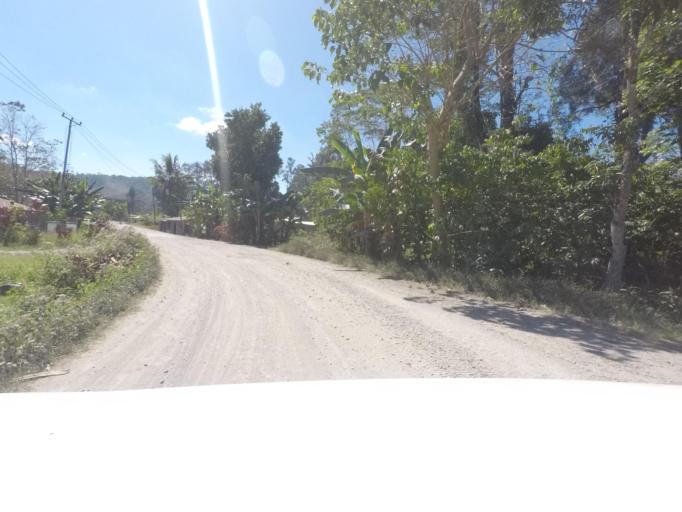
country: TL
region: Ermera
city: Gleno
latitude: -8.7177
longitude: 125.4303
